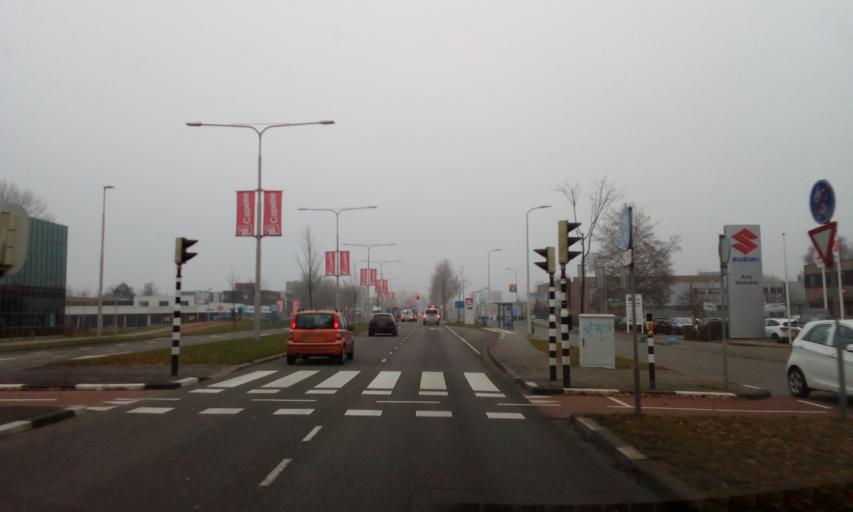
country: NL
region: South Holland
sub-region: Gemeente Capelle aan den IJssel
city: Capelle aan den IJssel
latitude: 51.9570
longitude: 4.5780
